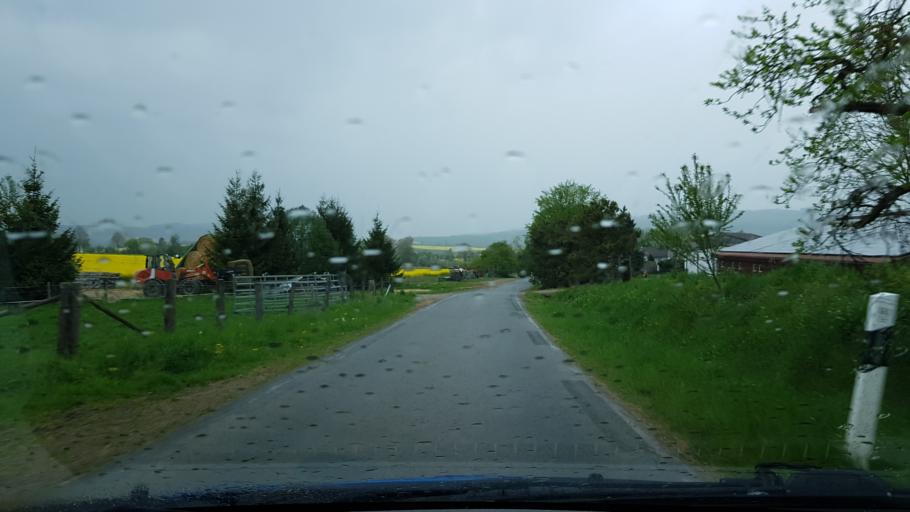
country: DE
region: Lower Saxony
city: Einbeck
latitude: 51.8631
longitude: 9.8794
